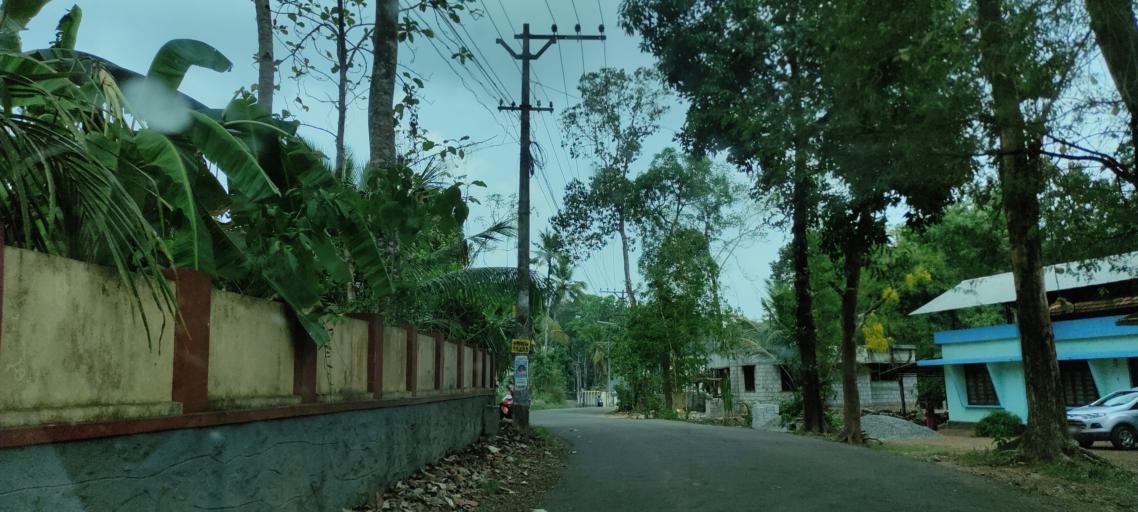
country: IN
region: Kerala
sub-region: Pattanamtitta
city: Adur
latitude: 9.1704
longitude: 76.7364
